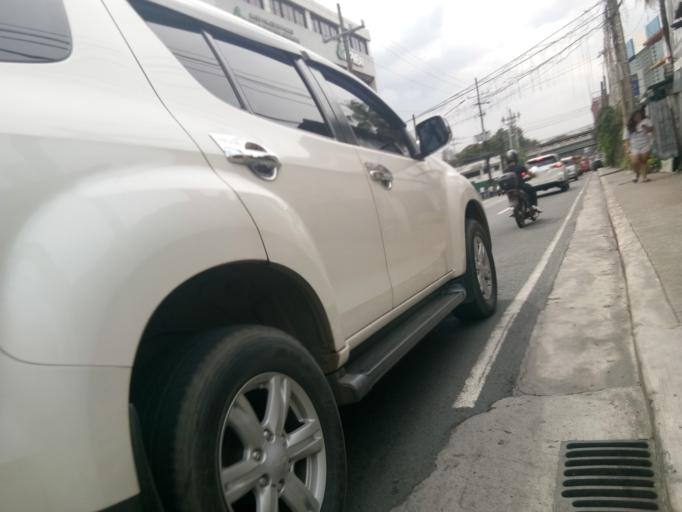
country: PH
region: Metro Manila
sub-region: Pasig
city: Pasig City
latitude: 14.6115
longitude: 121.0565
